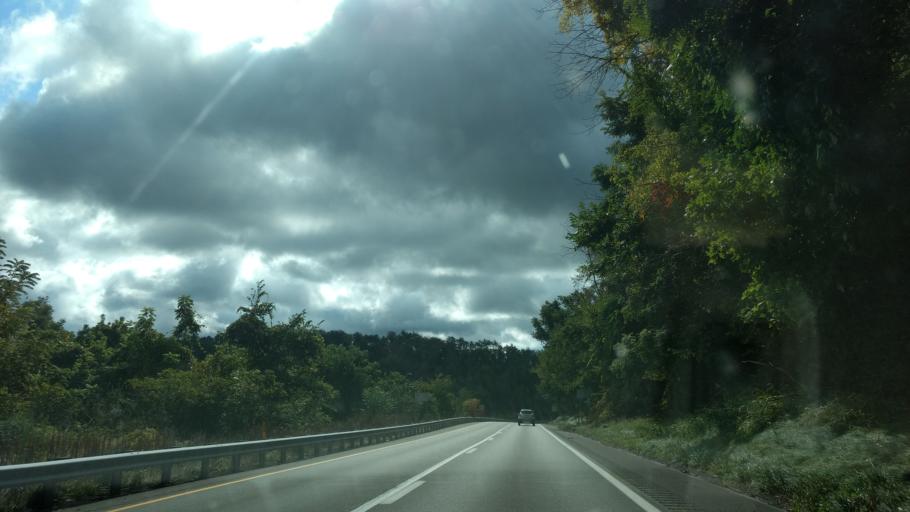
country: US
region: Pennsylvania
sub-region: Westmoreland County
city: Fellsburg
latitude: 40.1928
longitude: -79.8231
